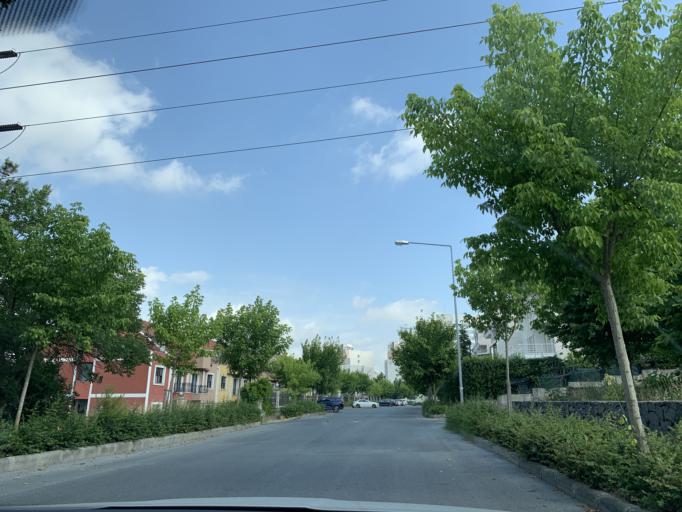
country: TR
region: Istanbul
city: Esenyurt
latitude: 41.0811
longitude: 28.6757
